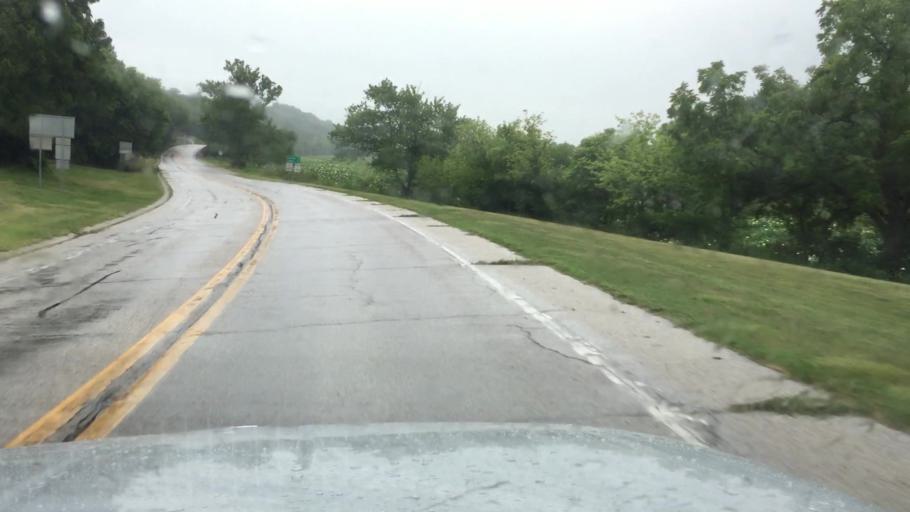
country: US
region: Illinois
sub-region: Hancock County
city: Nauvoo
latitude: 40.5388
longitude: -91.3853
